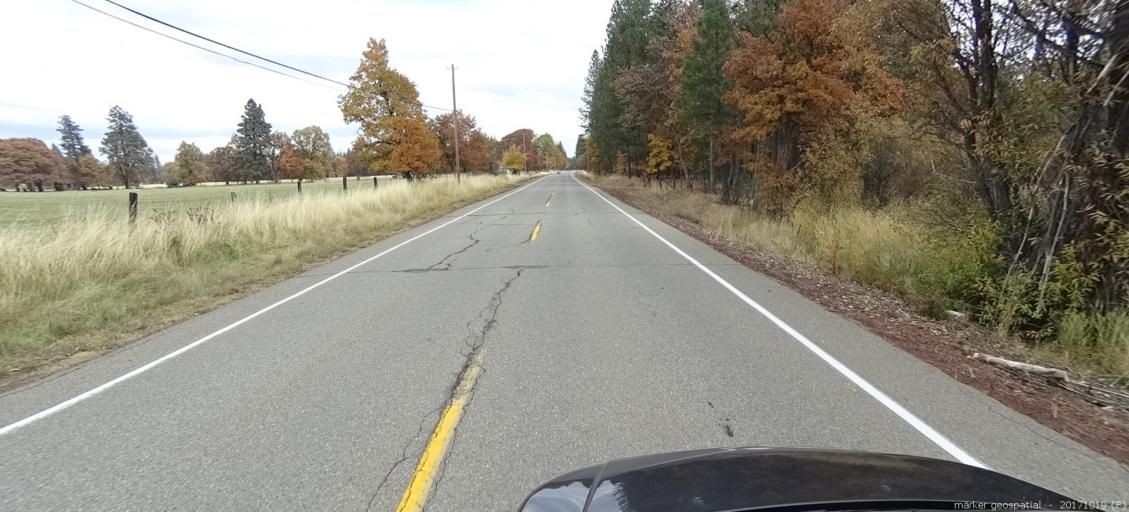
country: US
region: California
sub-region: Shasta County
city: Burney
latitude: 41.0945
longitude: -121.5459
